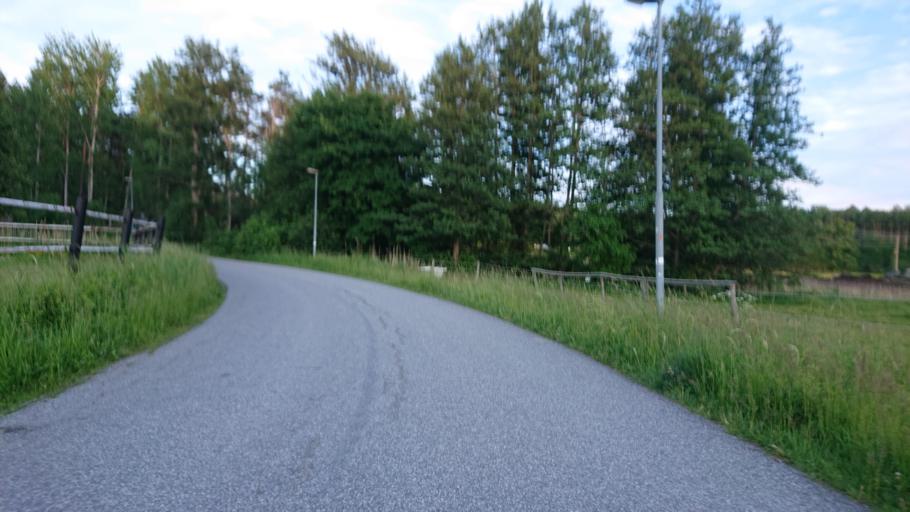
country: SE
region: Stockholm
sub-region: Osterakers Kommun
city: Akersberga
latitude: 59.5012
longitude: 18.3113
